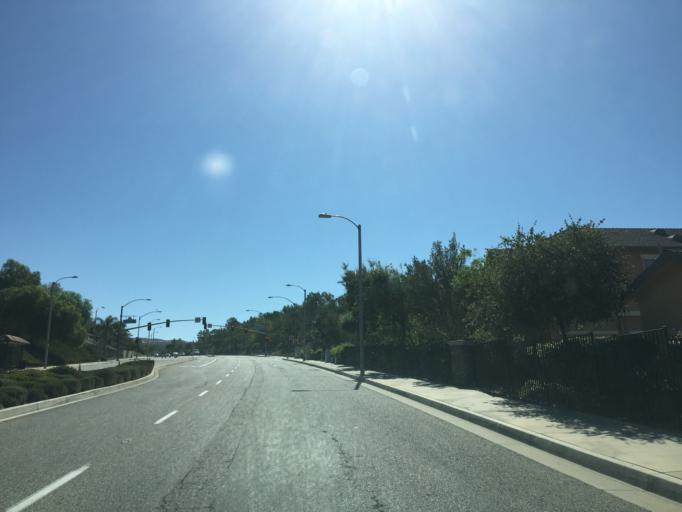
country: US
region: California
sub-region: Los Angeles County
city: Santa Clarita
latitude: 34.4460
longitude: -118.4849
